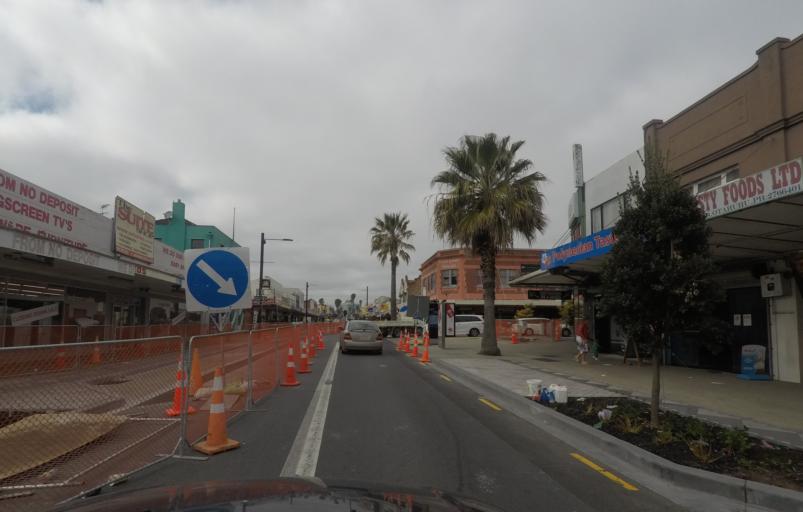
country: NZ
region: Auckland
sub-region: Auckland
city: Mangere
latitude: -36.9419
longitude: 174.8415
